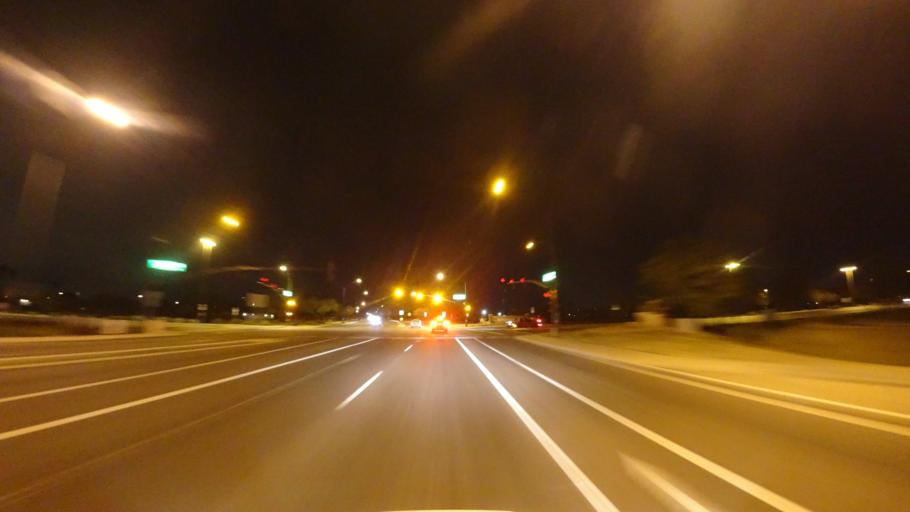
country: US
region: Arizona
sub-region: Maricopa County
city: Gilbert
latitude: 33.3353
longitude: -111.7382
